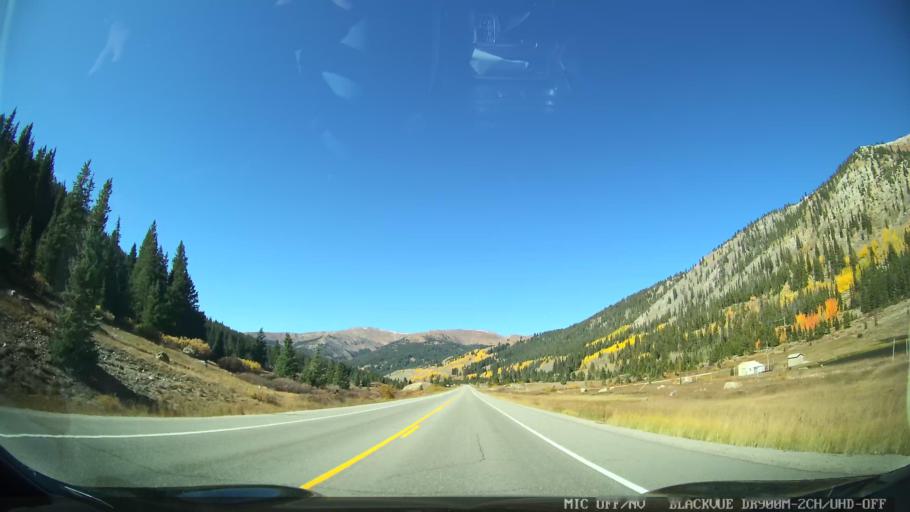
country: US
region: Colorado
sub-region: Lake County
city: Leadville
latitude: 39.3616
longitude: -106.1930
